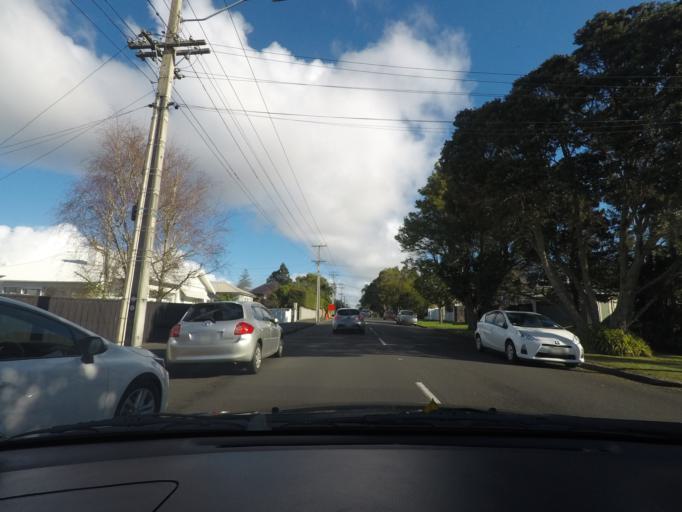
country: NZ
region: Auckland
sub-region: Auckland
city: Auckland
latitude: -36.8846
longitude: 174.7821
